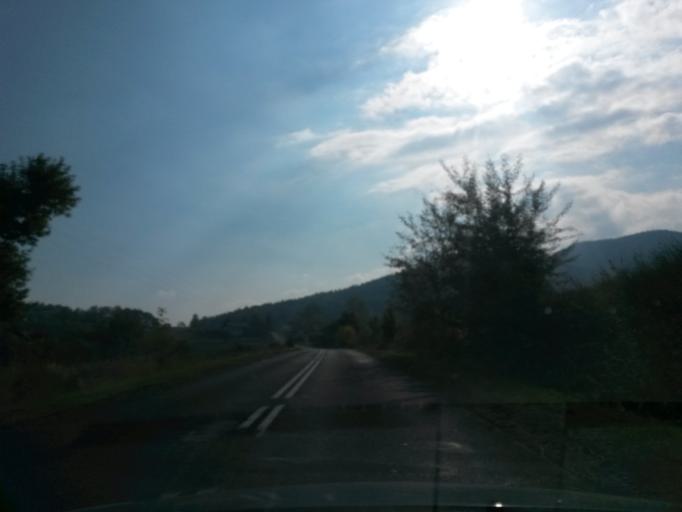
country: PL
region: Lower Silesian Voivodeship
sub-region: Powiat jeleniogorski
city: Sosnowka
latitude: 50.8232
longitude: 15.7275
